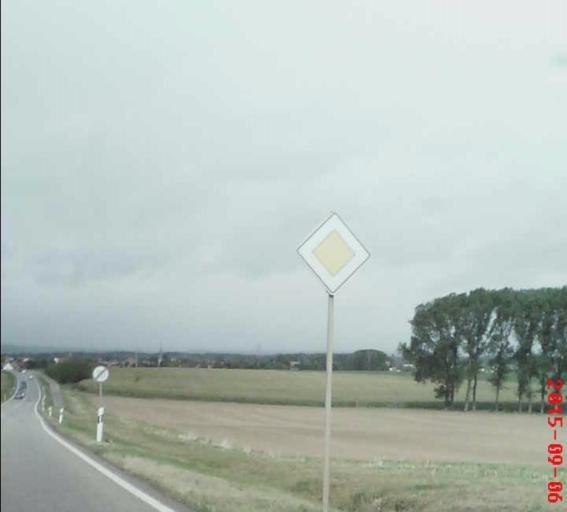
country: DE
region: Thuringia
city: Schonstedt
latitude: 51.1343
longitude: 10.5721
